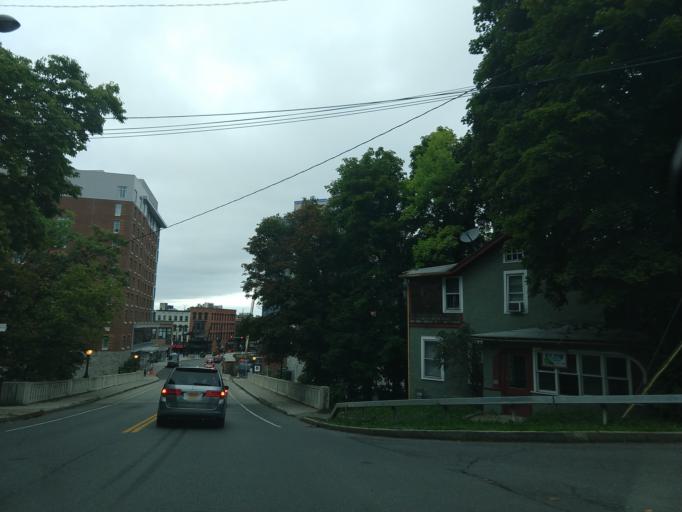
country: US
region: New York
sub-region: Tompkins County
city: Ithaca
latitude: 42.4384
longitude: -76.4949
